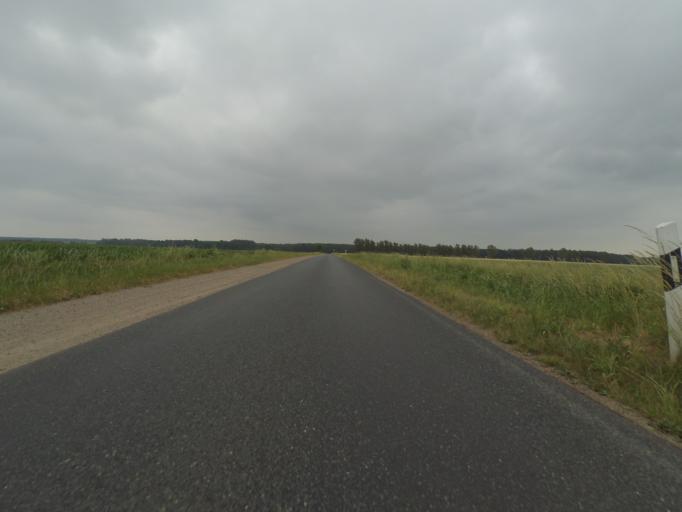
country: DE
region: Mecklenburg-Vorpommern
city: Spornitz
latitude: 53.3627
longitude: 11.6850
